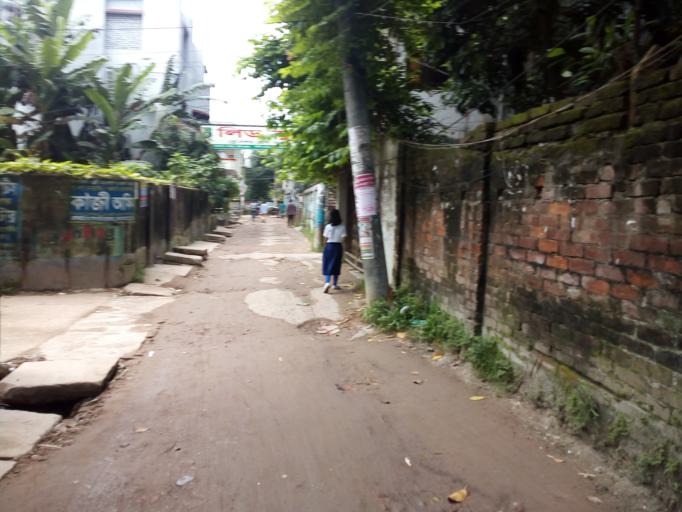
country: BD
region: Dhaka
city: Tungi
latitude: 23.8404
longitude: 90.2544
